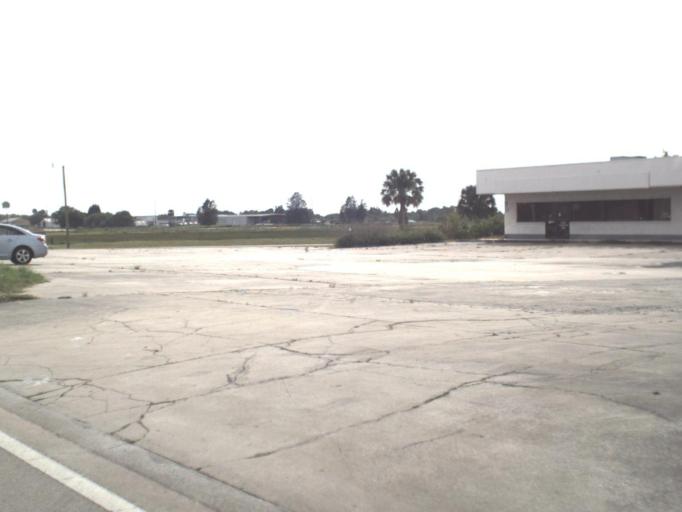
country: US
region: Florida
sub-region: Okeechobee County
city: Okeechobee
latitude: 27.2033
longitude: -80.8299
